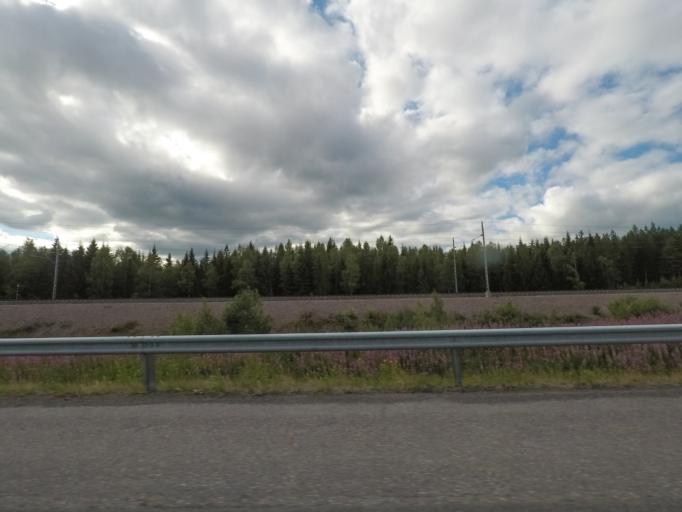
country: FI
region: Uusimaa
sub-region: Helsinki
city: Maentsaelae
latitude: 60.5798
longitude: 25.2145
